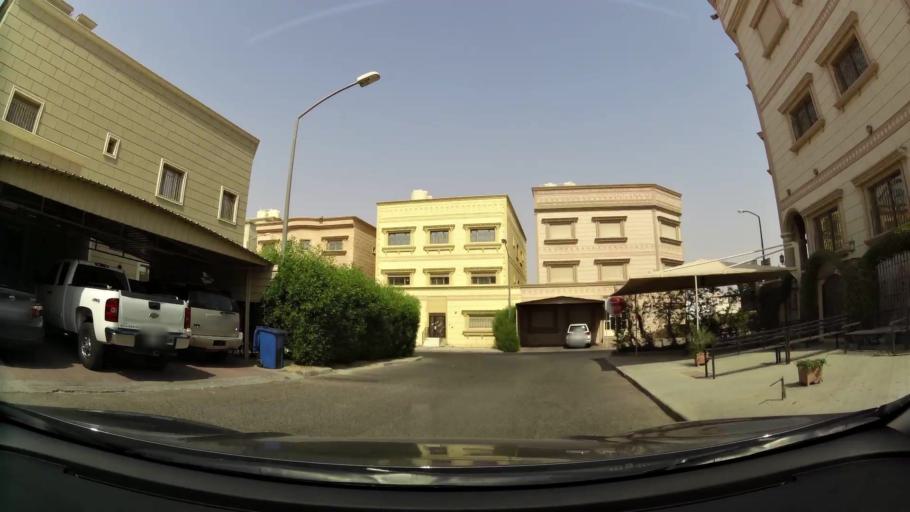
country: KW
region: Muhafazat al Jahra'
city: Al Jahra'
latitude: 29.3029
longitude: 47.7153
